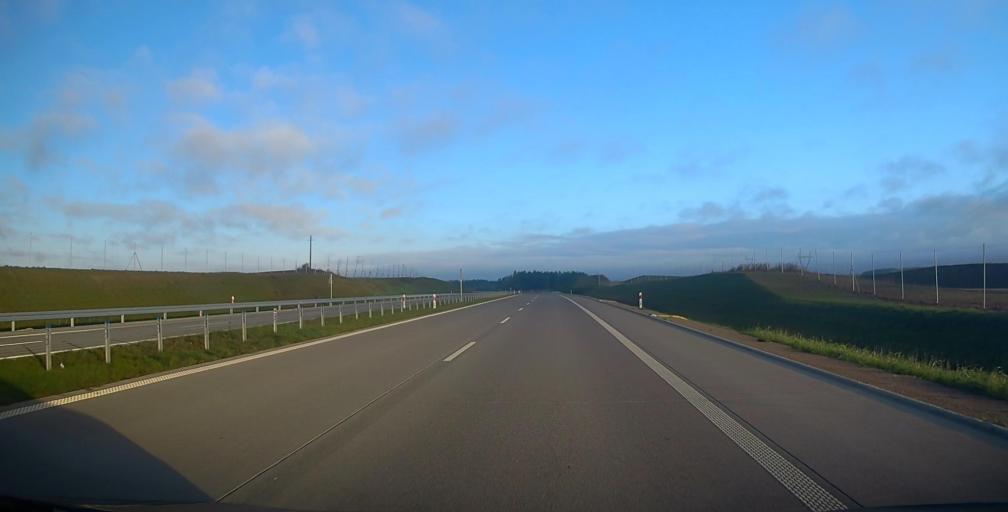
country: PL
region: Podlasie
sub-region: Powiat grajewski
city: Szczuczyn
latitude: 53.6827
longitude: 22.2955
